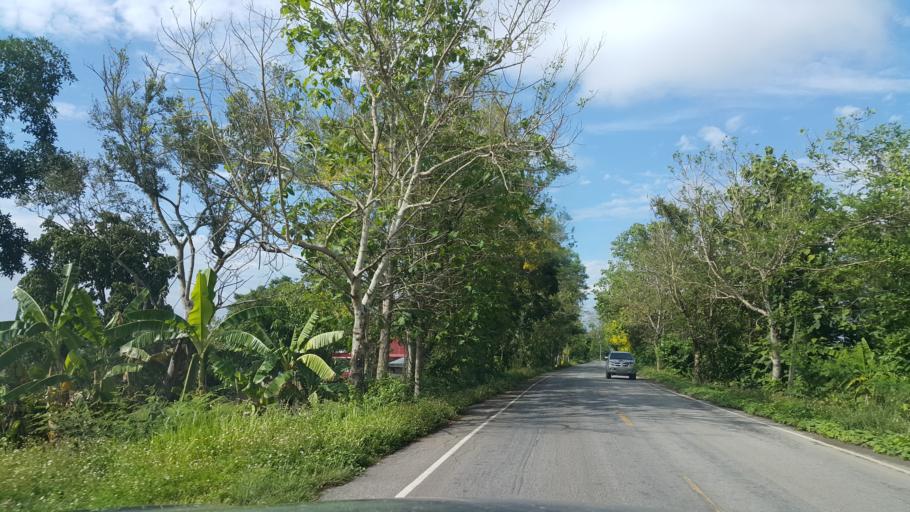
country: TH
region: Chiang Rai
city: Wiang Chai
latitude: 19.9309
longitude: 99.9073
